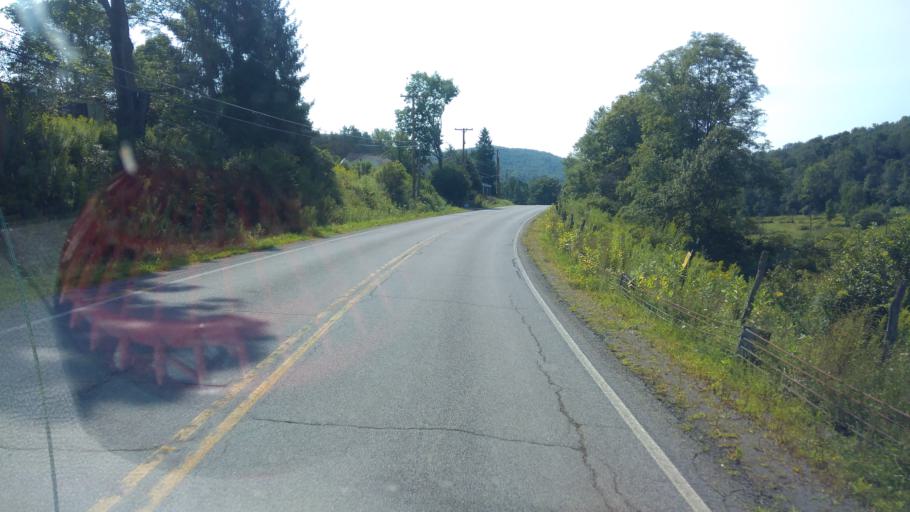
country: US
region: New York
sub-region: Allegany County
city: Bolivar
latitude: 42.0969
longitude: -78.1604
